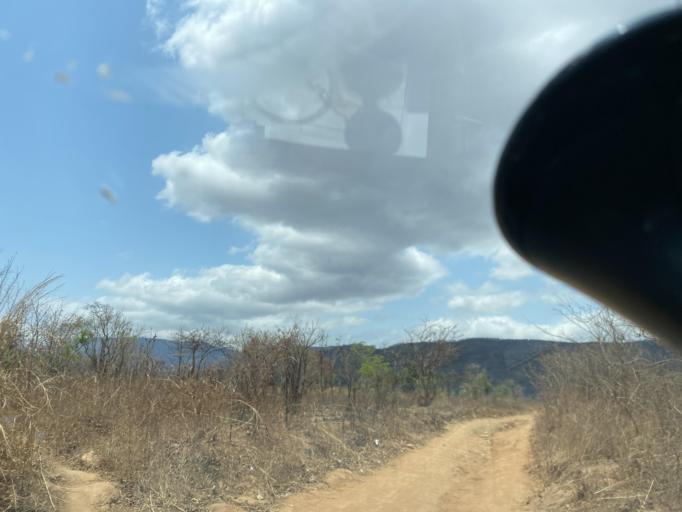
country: ZM
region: Lusaka
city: Luangwa
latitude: -15.1856
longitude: 29.7306
